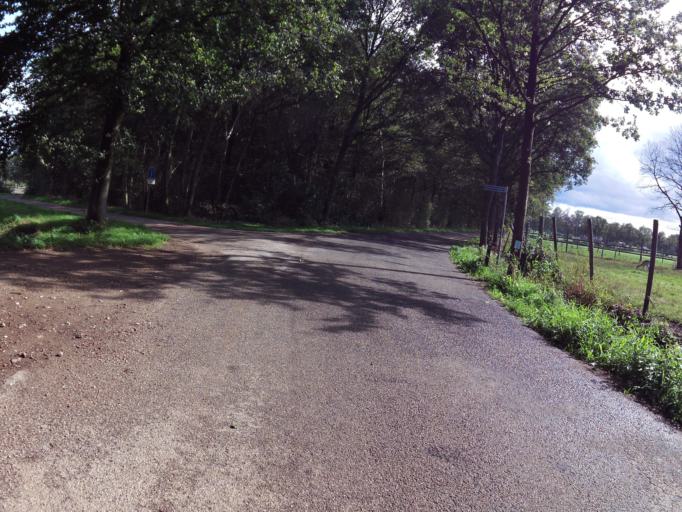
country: NL
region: Gelderland
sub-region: Gemeente Aalten
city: Bredevoort
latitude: 51.9582
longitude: 6.6248
